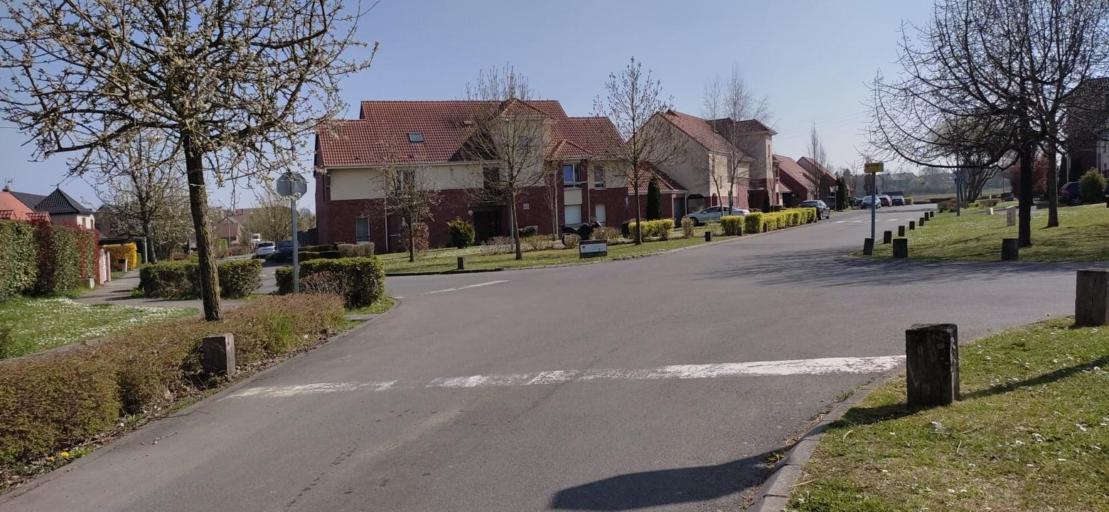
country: FR
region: Nord-Pas-de-Calais
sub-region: Departement du Pas-de-Calais
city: Aix-Noulette
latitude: 50.4381
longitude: 2.7133
